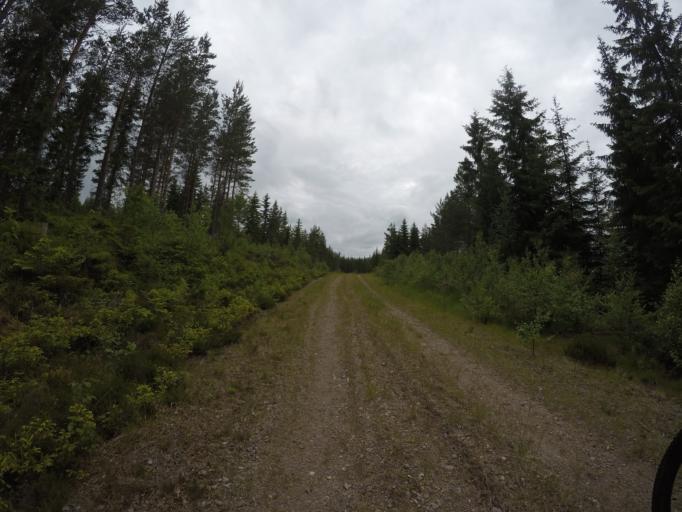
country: SE
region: Dalarna
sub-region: Ludvika Kommun
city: Abborrberget
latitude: 60.0783
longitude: 14.5235
